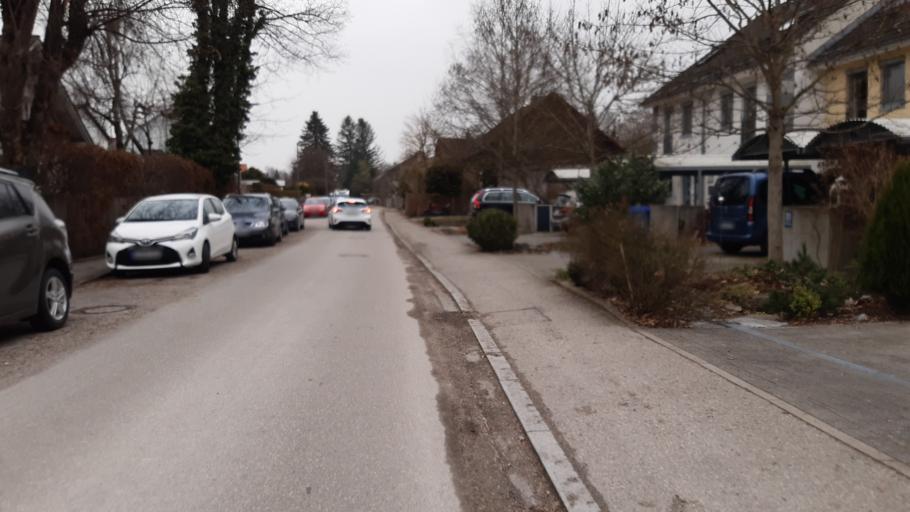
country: DE
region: Bavaria
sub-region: Upper Bavaria
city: Karlsfeld
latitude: 48.1958
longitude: 11.5164
